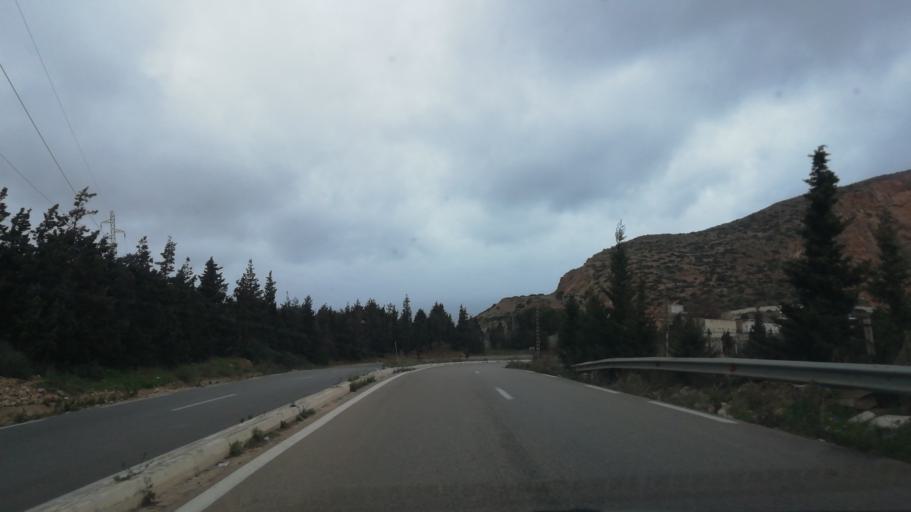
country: DZ
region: Oran
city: Mers el Kebir
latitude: 35.7201
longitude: -0.7352
